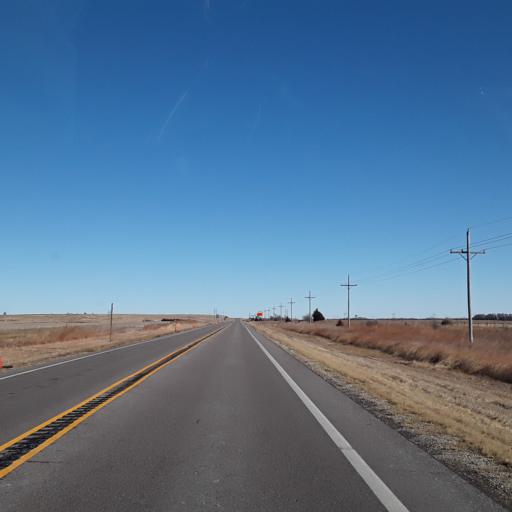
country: US
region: Kansas
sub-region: Pawnee County
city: Larned
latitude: 38.0807
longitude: -99.2358
